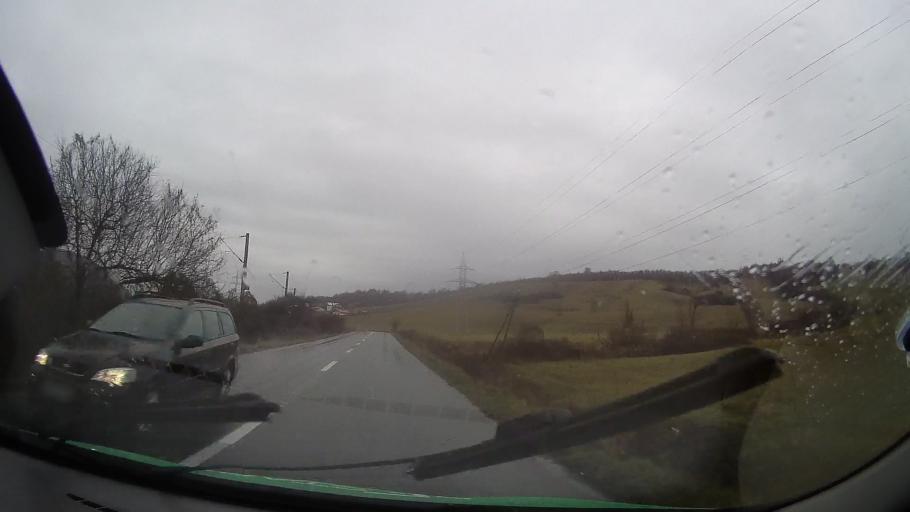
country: RO
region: Bistrita-Nasaud
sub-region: Municipiul Bistrita
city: Viisoara
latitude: 47.0469
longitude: 24.4635
